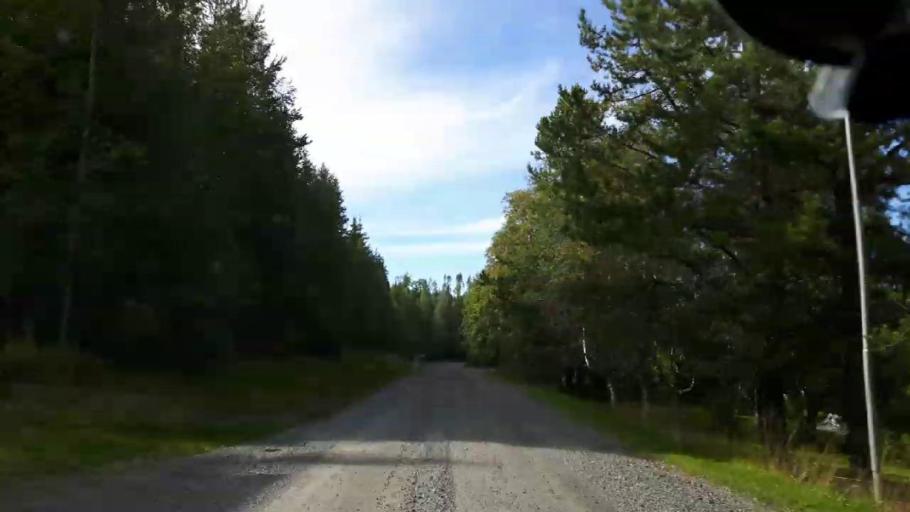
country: SE
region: Jaemtland
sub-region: Ragunda Kommun
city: Hammarstrand
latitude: 63.1331
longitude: 16.1209
